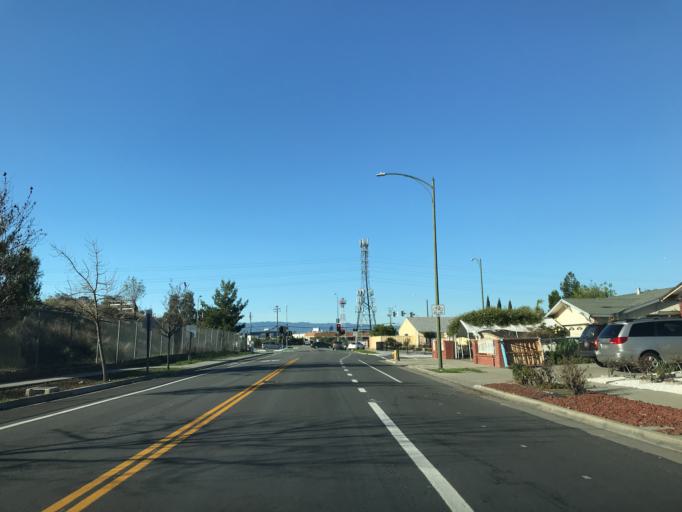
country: US
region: California
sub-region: Santa Clara County
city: Alum Rock
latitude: 37.3382
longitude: -121.8162
